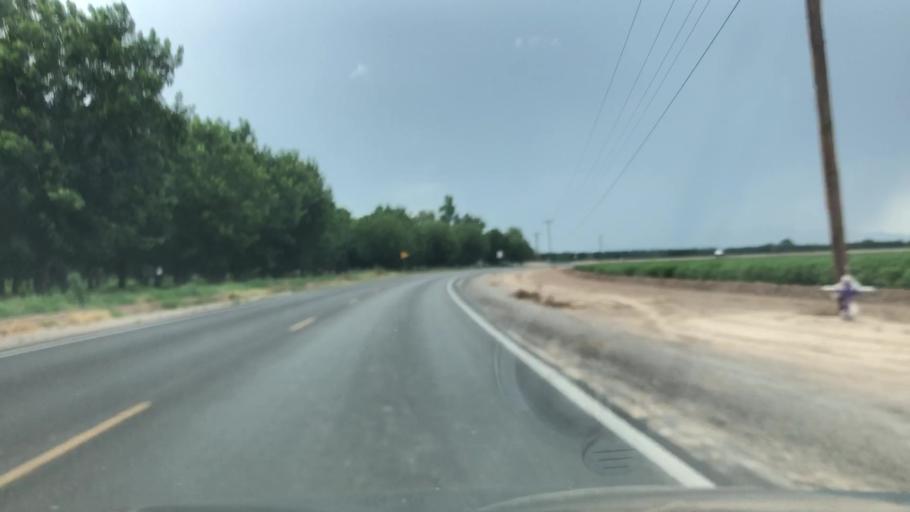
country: US
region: New Mexico
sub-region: Dona Ana County
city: La Union
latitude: 31.9715
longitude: -106.6519
